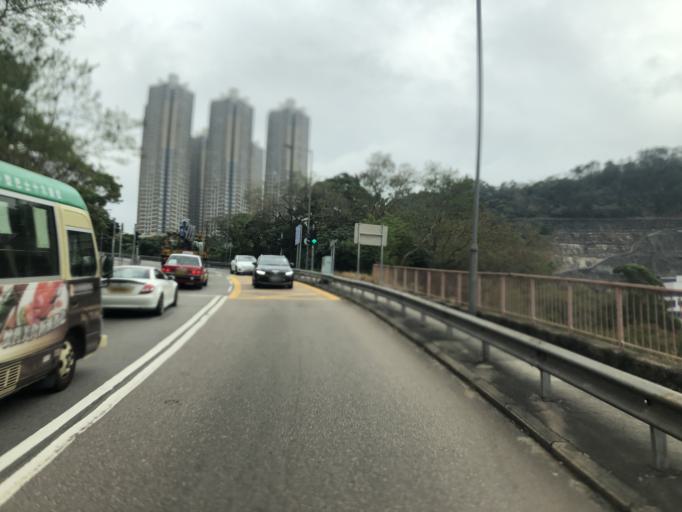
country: HK
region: Wong Tai Sin
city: Wong Tai Sin
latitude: 22.3340
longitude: 114.2179
